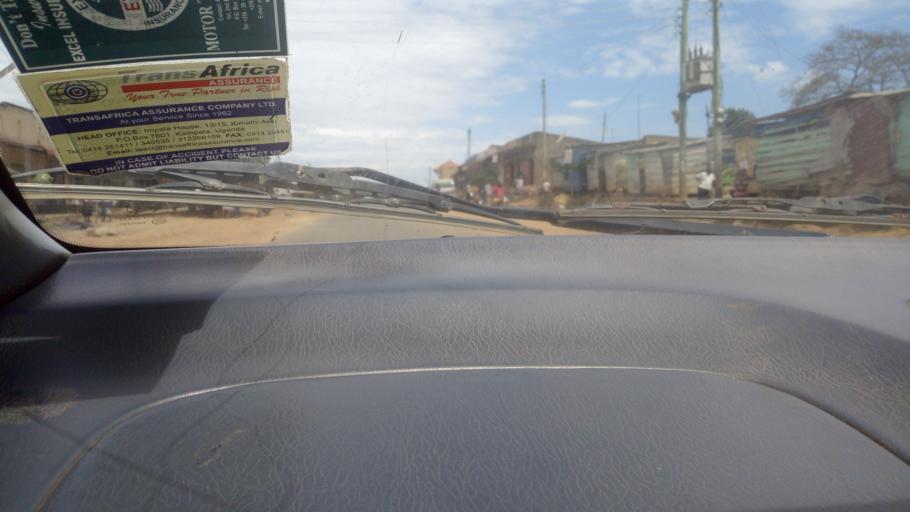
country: UG
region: Western Region
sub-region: Mbarara District
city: Bwizibwera
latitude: -0.4085
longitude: 30.5685
